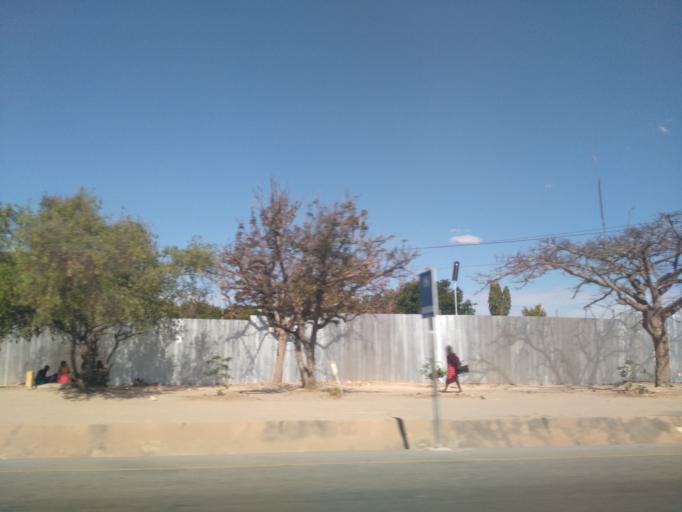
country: TZ
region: Dodoma
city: Dodoma
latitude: -6.1827
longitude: 35.7466
